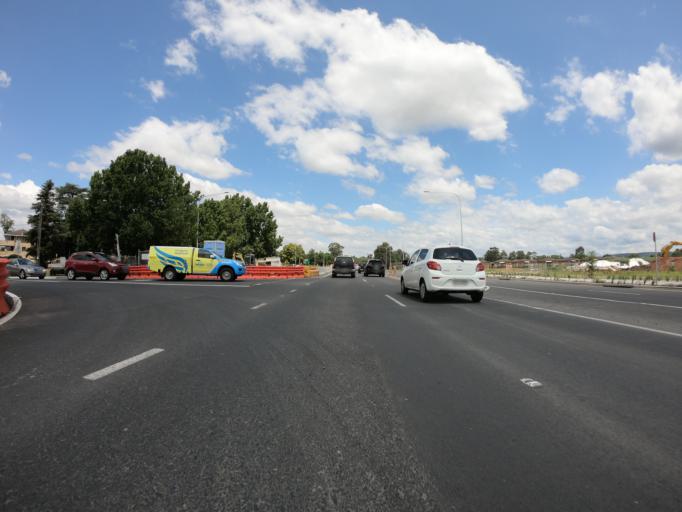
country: AU
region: New South Wales
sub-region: Penrith Municipality
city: Penrith
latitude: -33.7520
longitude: 150.6874
